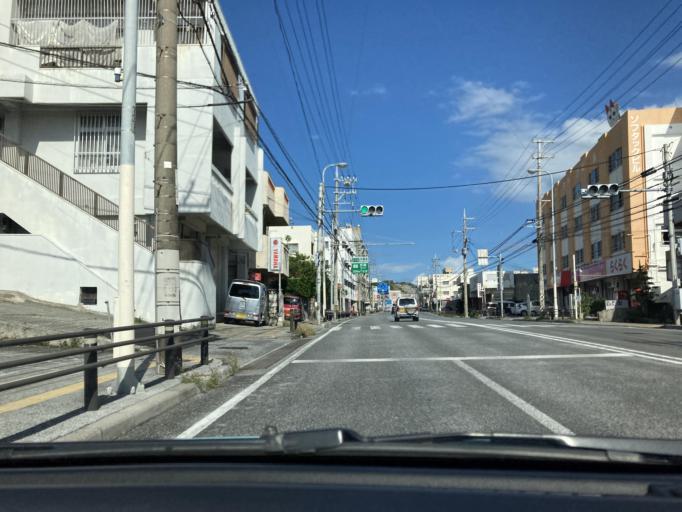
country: JP
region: Okinawa
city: Tomigusuku
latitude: 26.1978
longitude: 127.7095
